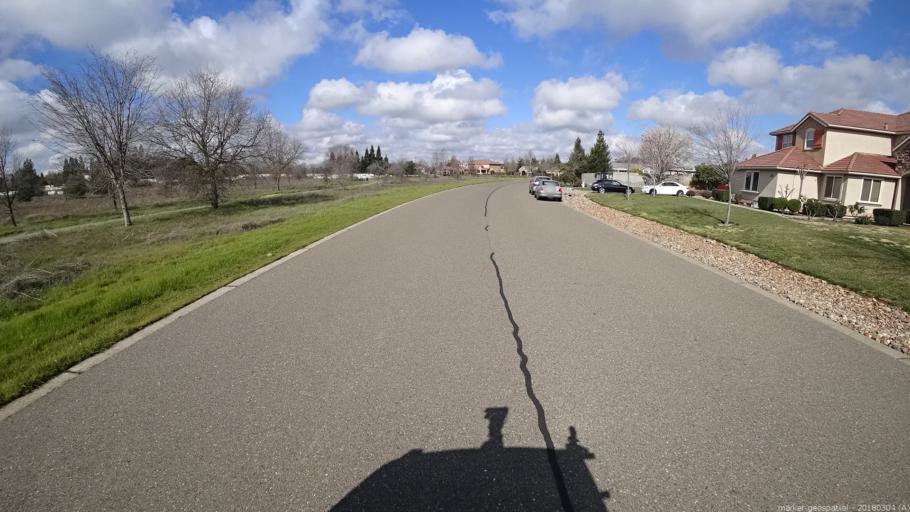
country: US
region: California
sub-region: Sacramento County
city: Vineyard
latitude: 38.4639
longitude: -121.3136
